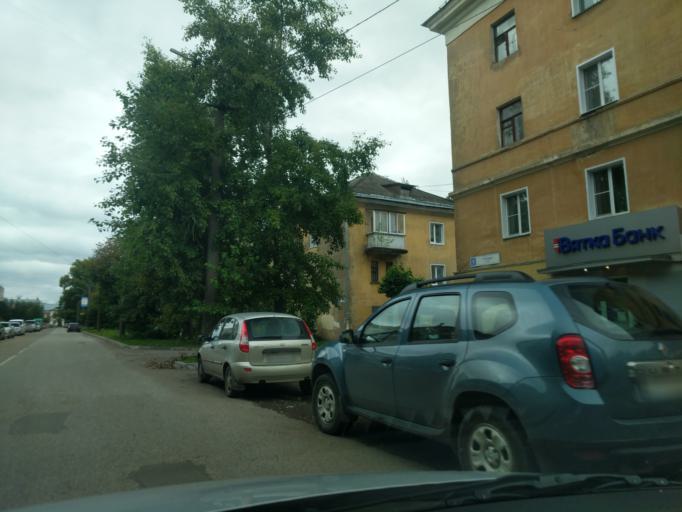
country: RU
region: Kirov
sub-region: Kirovo-Chepetskiy Rayon
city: Kirov
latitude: 58.6372
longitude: 49.6191
